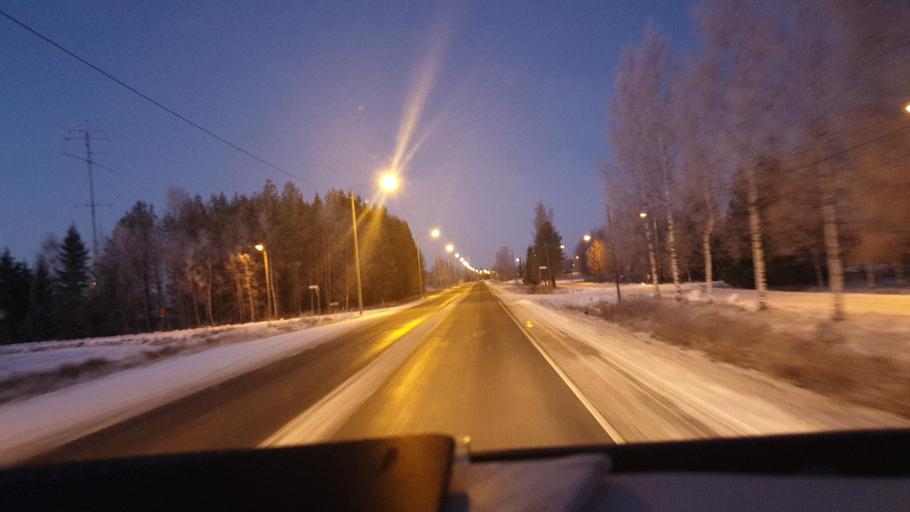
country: FI
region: Northern Ostrobothnia
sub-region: Raahe
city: Raahe
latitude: 64.6887
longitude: 24.6094
